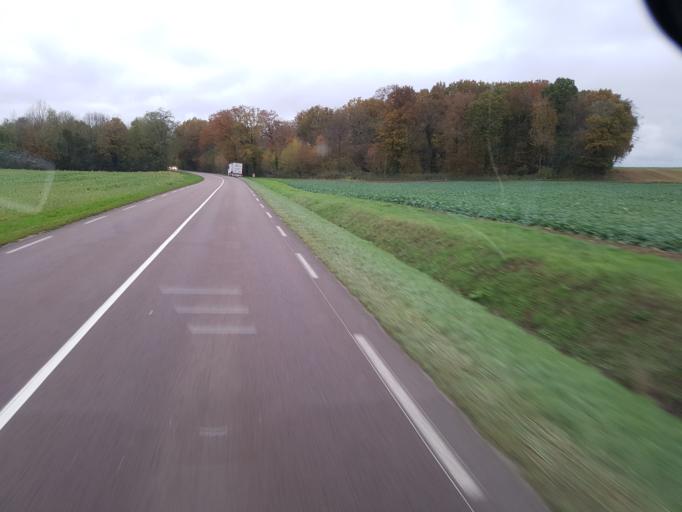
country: FR
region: Champagne-Ardenne
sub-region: Departement de la Marne
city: Esternay
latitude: 48.7930
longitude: 3.6311
